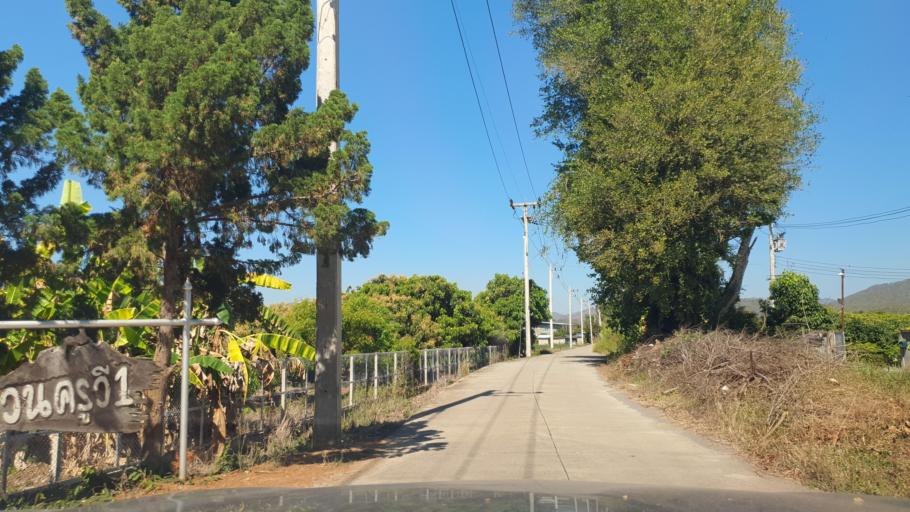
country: TH
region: Chiang Mai
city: Mae Wang
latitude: 18.6592
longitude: 98.8302
